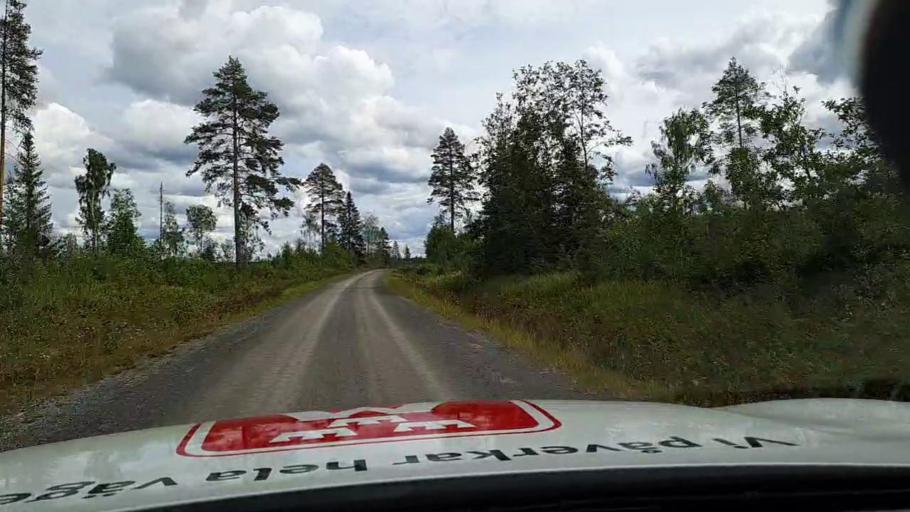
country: SE
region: Jaemtland
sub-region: OEstersunds Kommun
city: Lit
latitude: 63.2973
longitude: 15.3284
